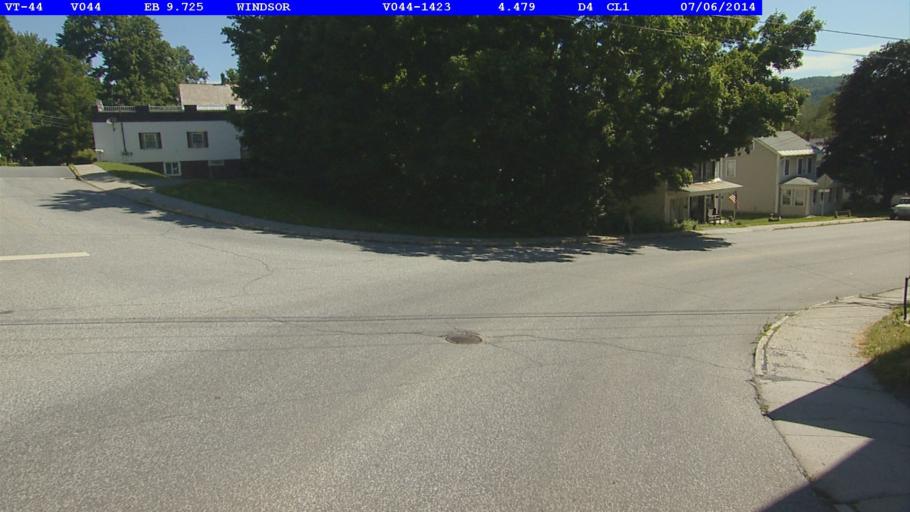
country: US
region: Vermont
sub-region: Windsor County
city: Windsor
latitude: 43.4780
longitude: -72.3966
